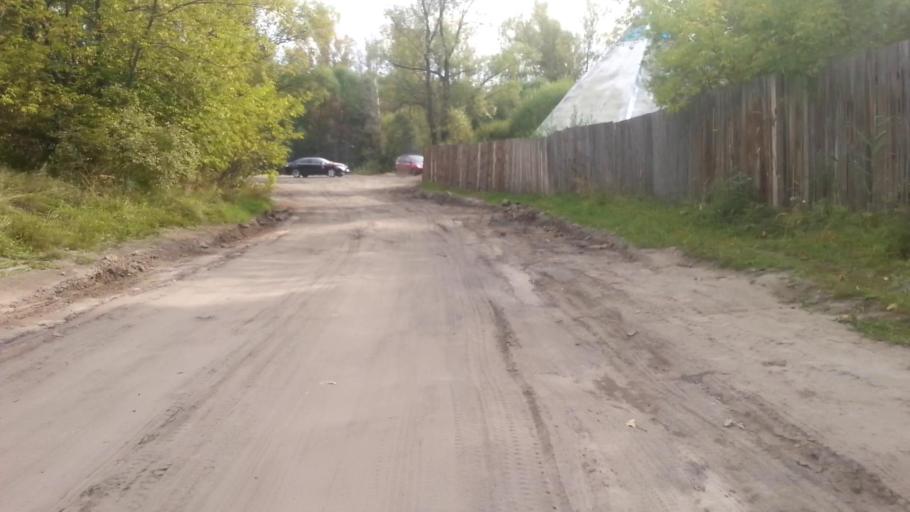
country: RU
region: Altai Krai
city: Yuzhnyy
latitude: 53.3070
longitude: 83.7005
